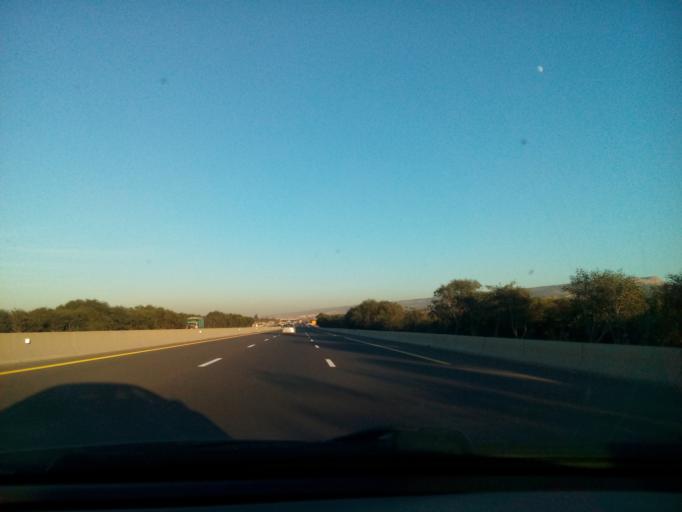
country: DZ
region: Relizane
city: Oued Rhiou
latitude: 35.9785
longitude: 0.9273
